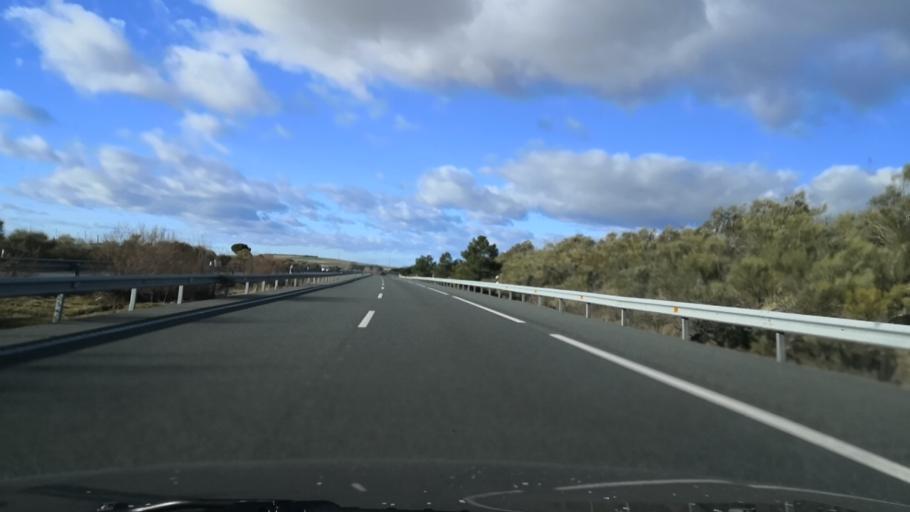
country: ES
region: Castille and Leon
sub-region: Provincia de Avila
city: Adanero
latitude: 40.9303
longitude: -4.5828
